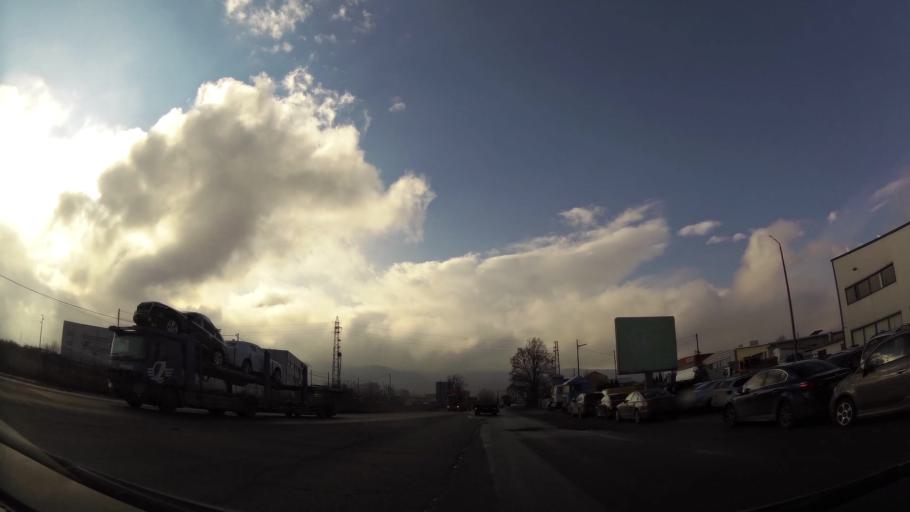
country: BG
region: Sofia-Capital
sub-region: Stolichna Obshtina
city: Sofia
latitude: 42.6281
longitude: 23.4463
